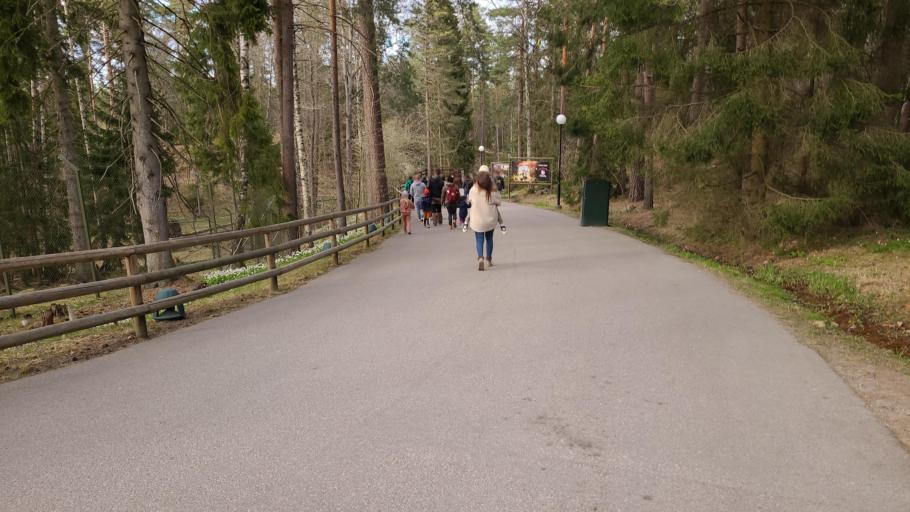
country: SE
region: OEstergoetland
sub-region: Norrkopings Kommun
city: Krokek
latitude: 58.6641
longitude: 16.4621
